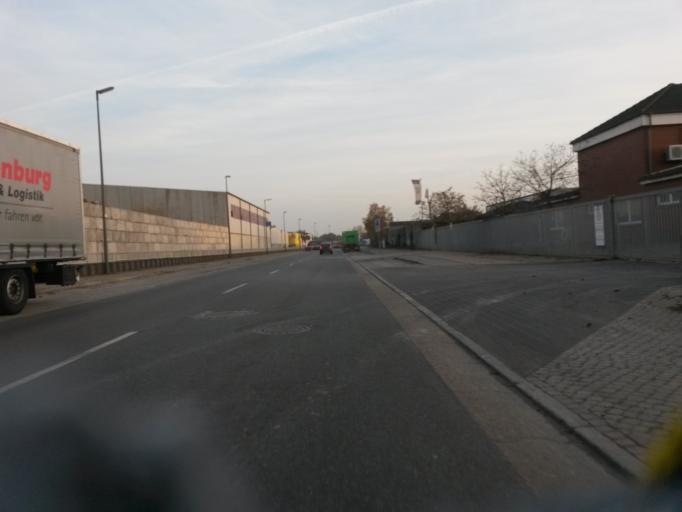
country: DE
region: Bremen
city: Bremen
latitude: 53.0550
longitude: 8.8799
